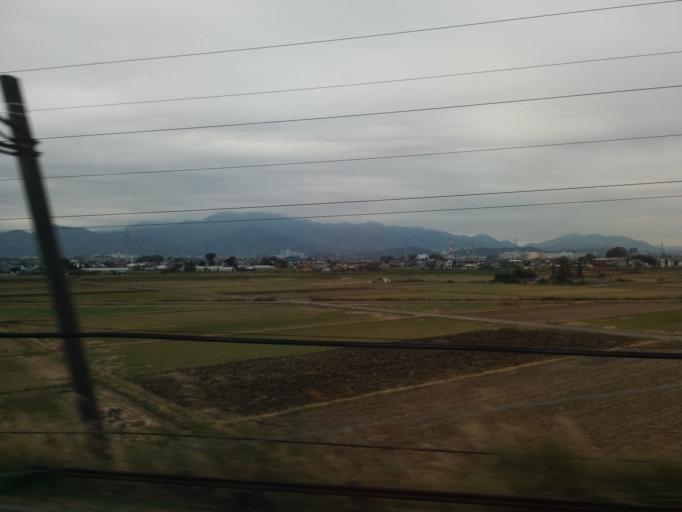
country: JP
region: Kanagawa
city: Isehara
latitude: 35.3841
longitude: 139.3599
